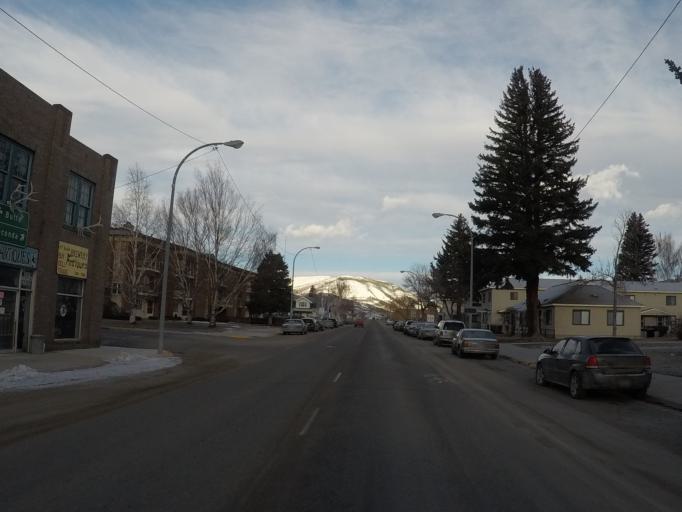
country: US
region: Montana
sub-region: Deer Lodge County
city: Anaconda
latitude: 46.1305
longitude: -112.9536
